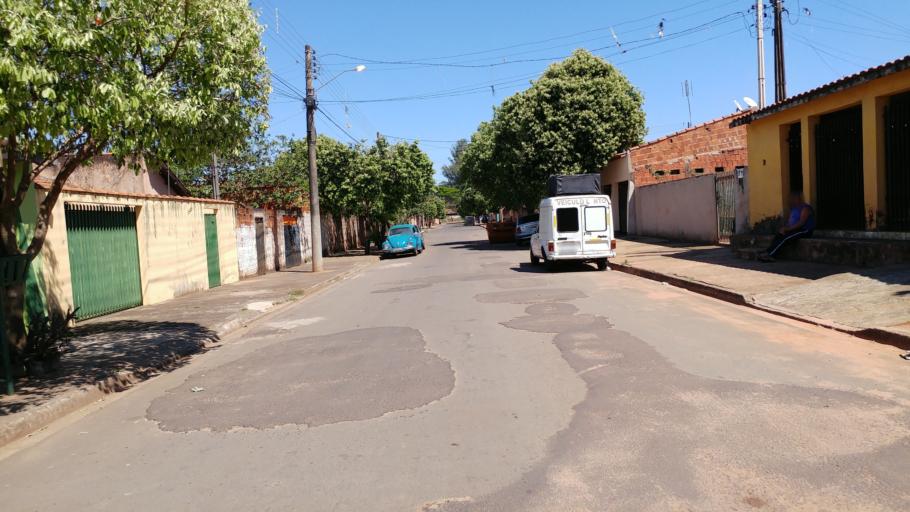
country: BR
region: Sao Paulo
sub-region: Paraguacu Paulista
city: Paraguacu Paulista
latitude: -22.4190
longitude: -50.5689
